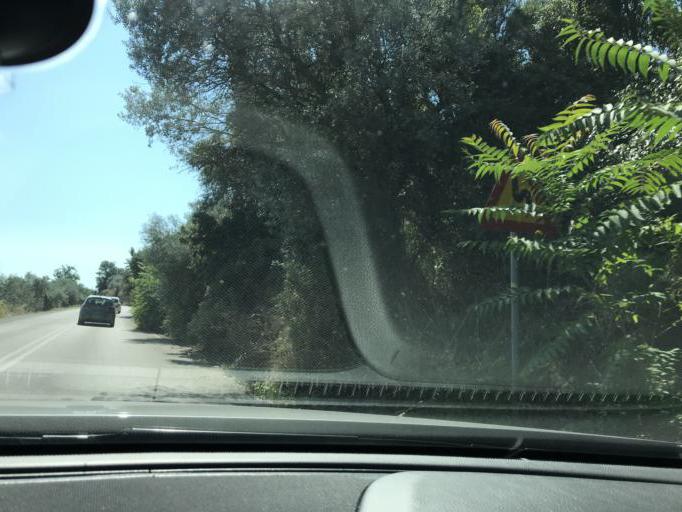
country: GR
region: Central Greece
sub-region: Nomos Fthiotidos
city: Kato Tithorea
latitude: 38.5186
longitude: 22.7374
